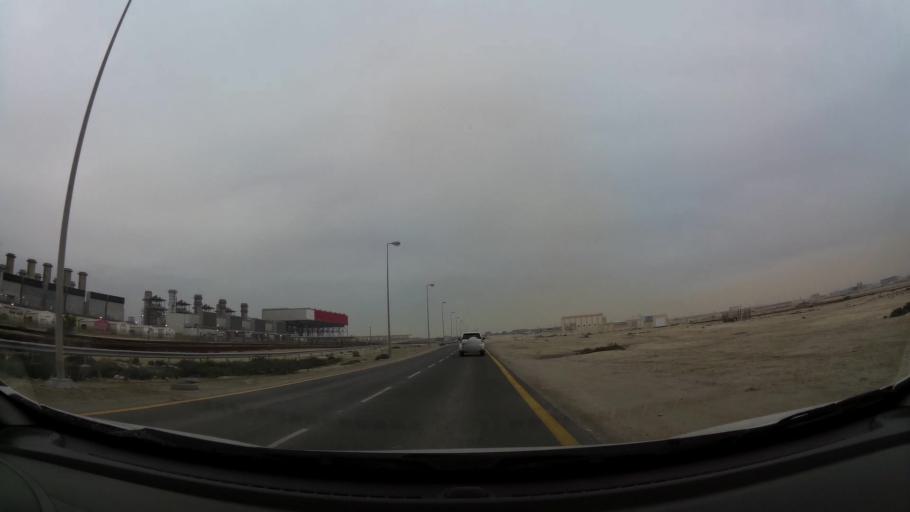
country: BH
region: Northern
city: Ar Rifa'
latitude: 26.0968
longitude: 50.6014
